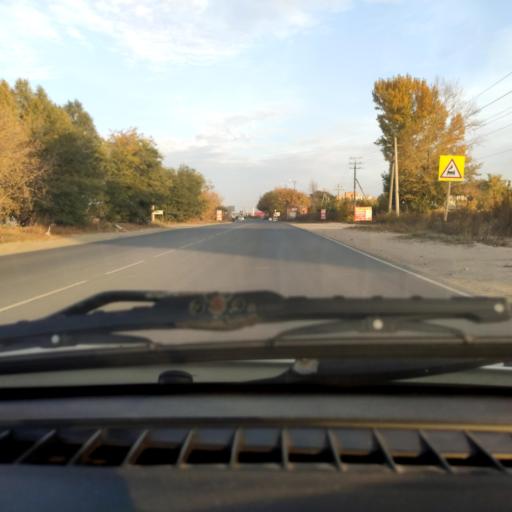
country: RU
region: Samara
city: Tol'yatti
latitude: 53.5302
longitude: 49.4661
